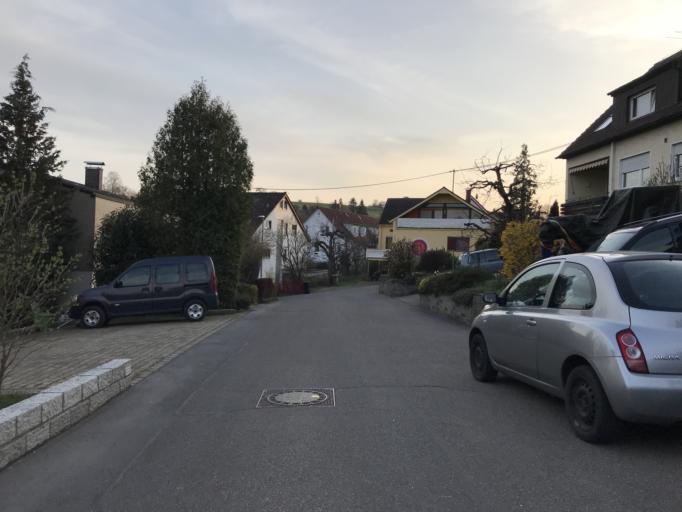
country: DE
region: Baden-Wuerttemberg
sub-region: Regierungsbezirk Stuttgart
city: Unterensingen
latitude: 48.6535
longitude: 9.3520
